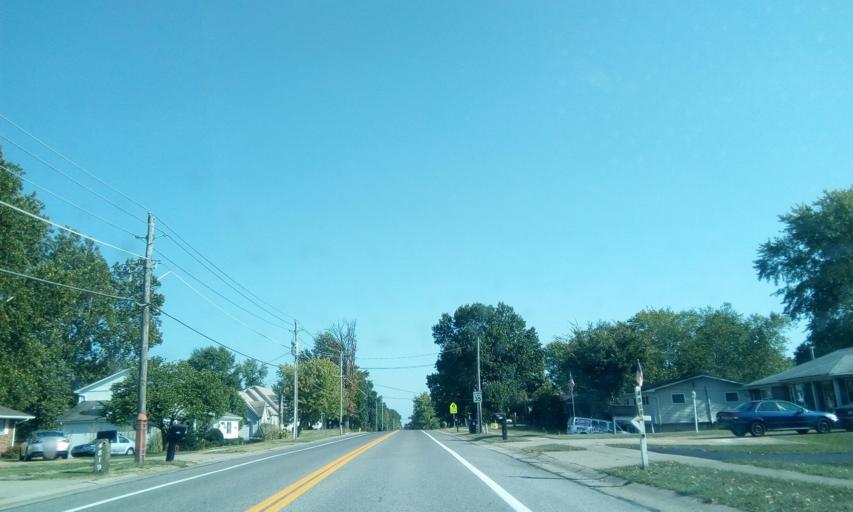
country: US
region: Missouri
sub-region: Saint Louis County
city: Concord
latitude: 38.5029
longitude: -90.3642
